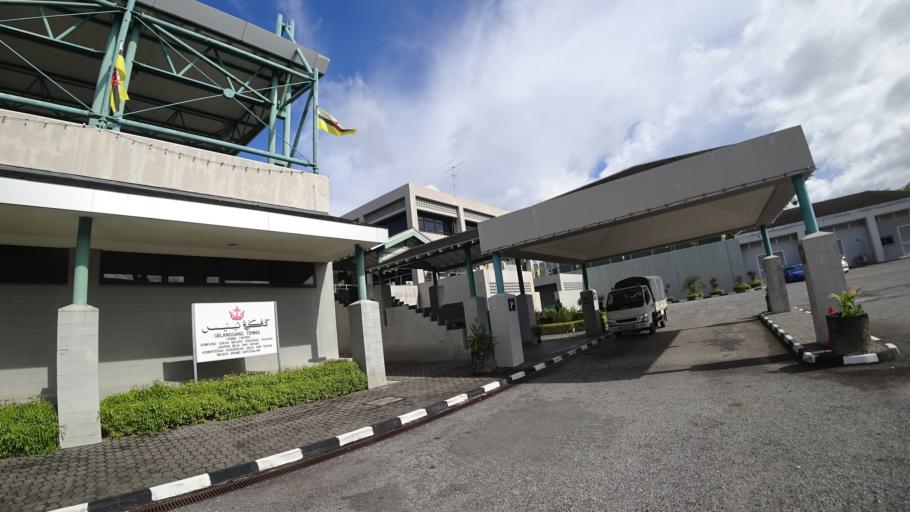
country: BN
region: Brunei and Muara
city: Bandar Seri Begawan
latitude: 4.9285
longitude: 114.9468
